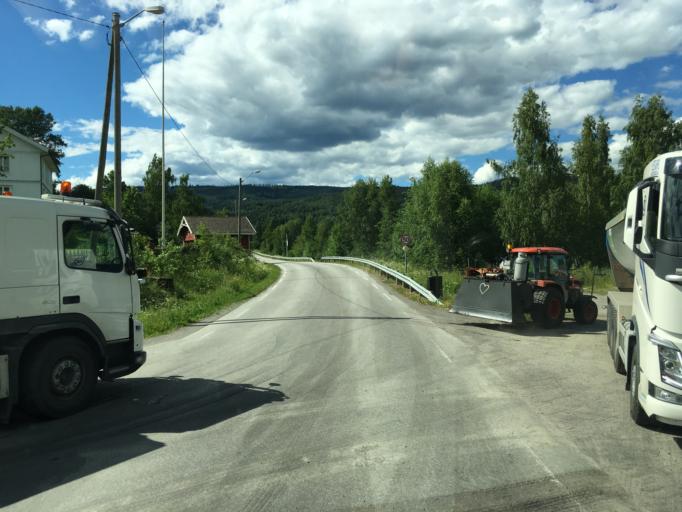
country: NO
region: Oppland
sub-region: Sondre Land
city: Hov
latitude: 60.5176
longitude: 10.2970
